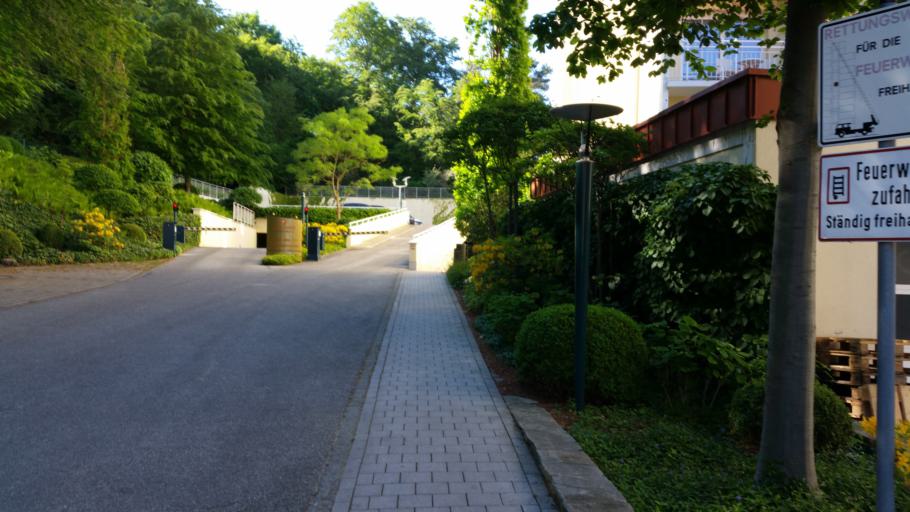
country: DE
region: Mecklenburg-Vorpommern
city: Seebad Bansin
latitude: 53.9767
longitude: 14.1391
